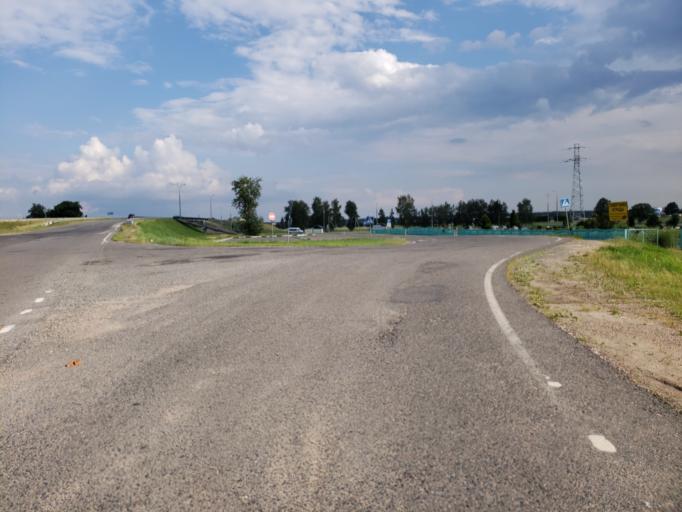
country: BY
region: Minsk
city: Chervyen'
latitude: 53.7261
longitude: 28.3919
